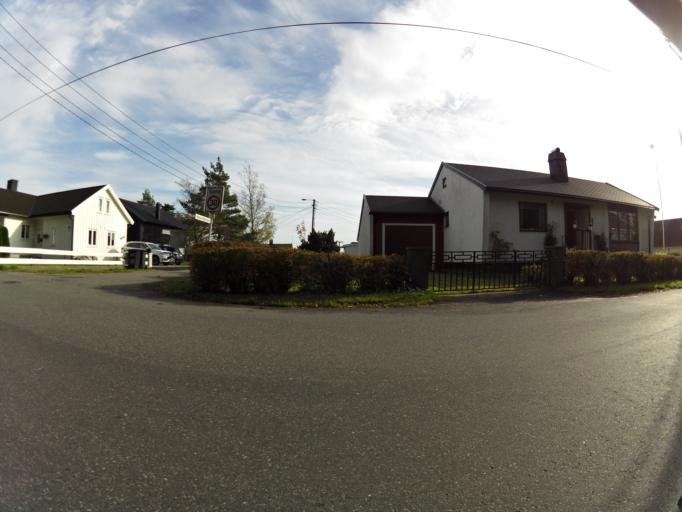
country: NO
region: Ostfold
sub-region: Fredrikstad
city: Fredrikstad
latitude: 59.2356
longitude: 10.9673
